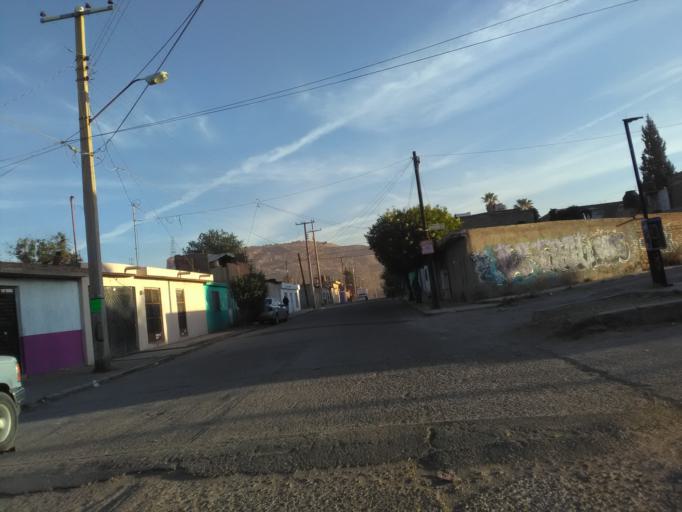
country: MX
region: Durango
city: Victoria de Durango
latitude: 24.0437
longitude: -104.6686
